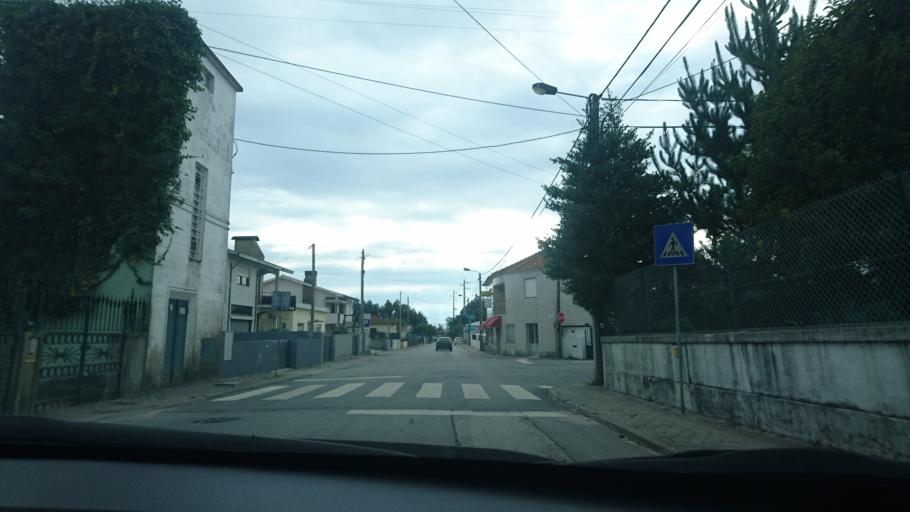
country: PT
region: Aveiro
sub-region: Ovar
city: Cortegaca
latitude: 40.9611
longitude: -8.6047
